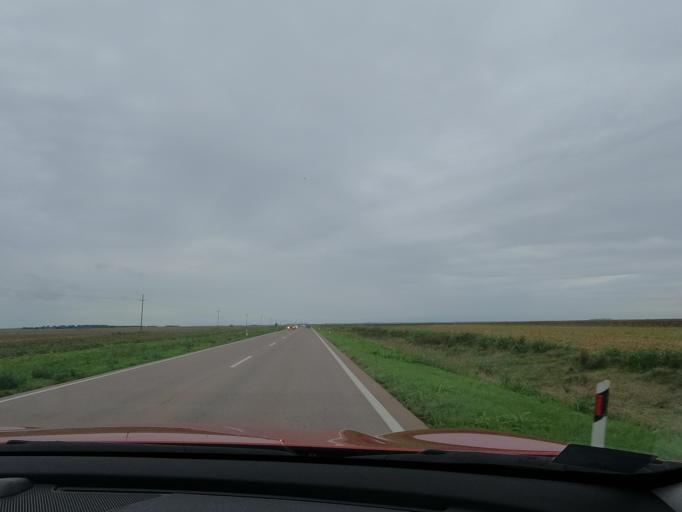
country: RS
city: Banatska Topola
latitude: 45.7269
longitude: 20.4185
